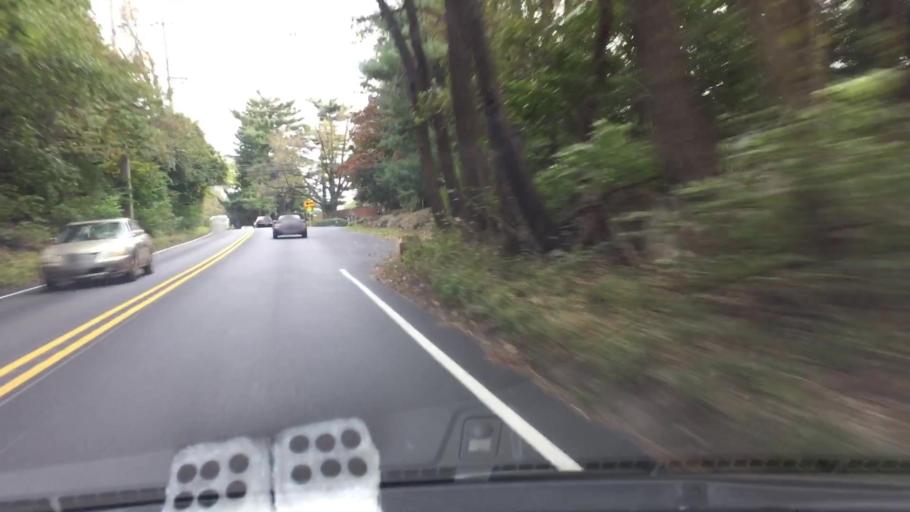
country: US
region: Pennsylvania
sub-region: Chester County
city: Malvern
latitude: 39.9725
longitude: -75.5325
